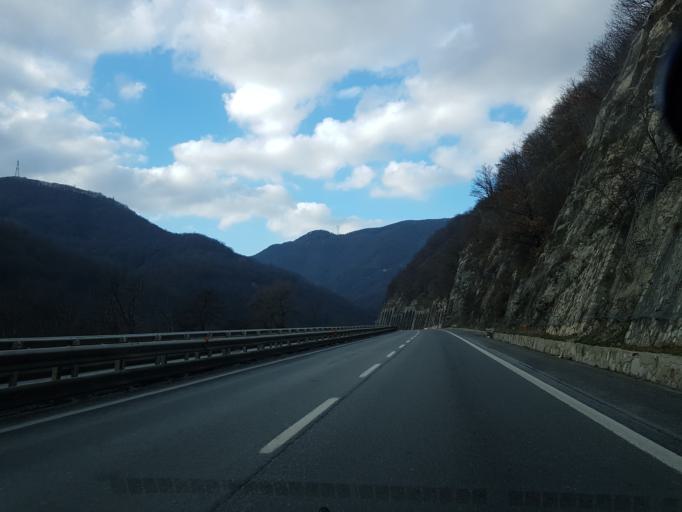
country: IT
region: Liguria
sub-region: Provincia di Genova
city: Ronco Scrivia
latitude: 44.6258
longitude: 8.9487
